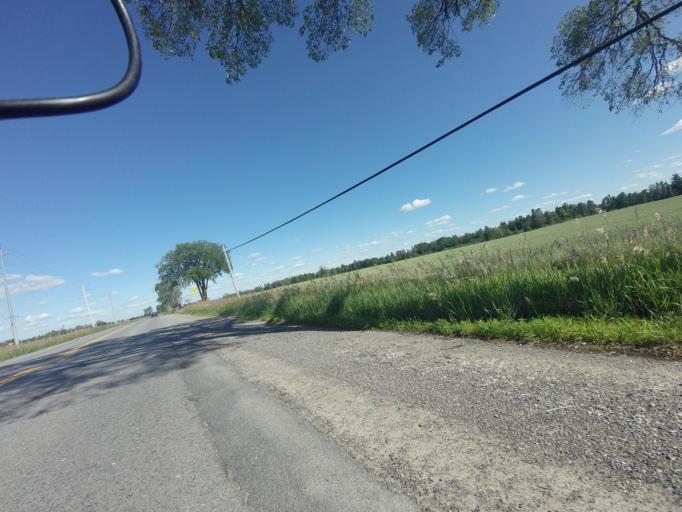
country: CA
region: Ontario
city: Arnprior
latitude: 45.4165
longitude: -76.4179
